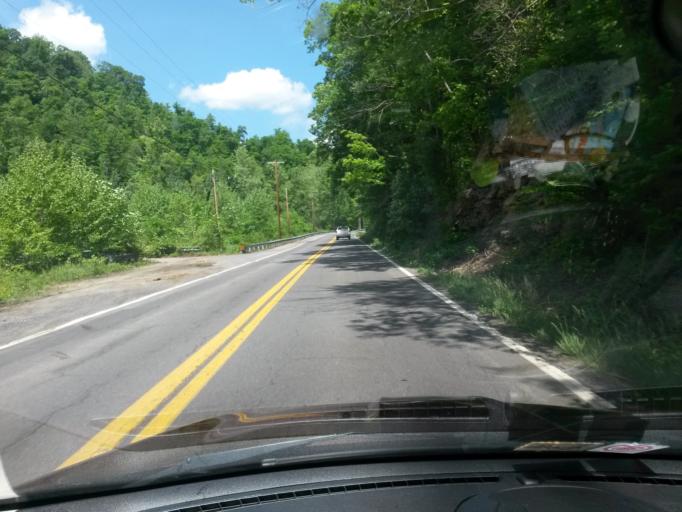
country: US
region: West Virginia
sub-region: McDowell County
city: Welch
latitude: 37.5127
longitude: -81.5788
